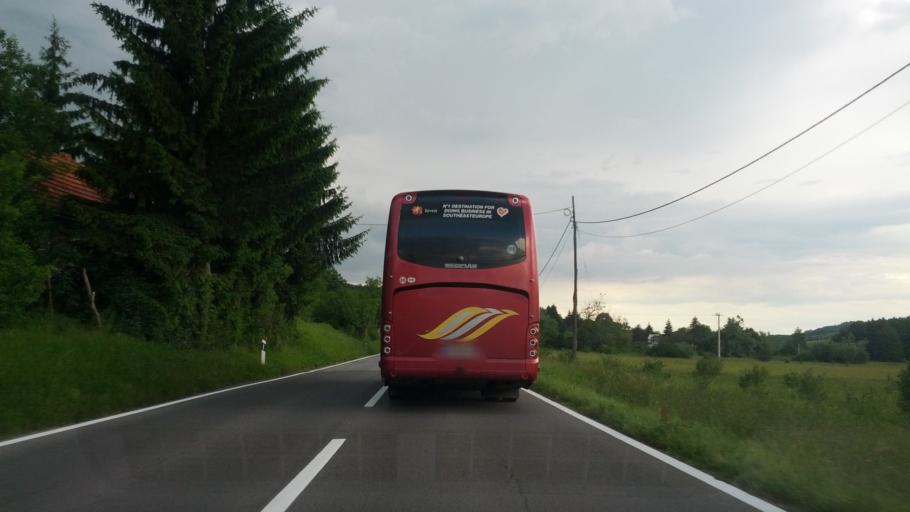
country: HR
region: Karlovacka
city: Vojnic
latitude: 45.3240
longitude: 15.6162
